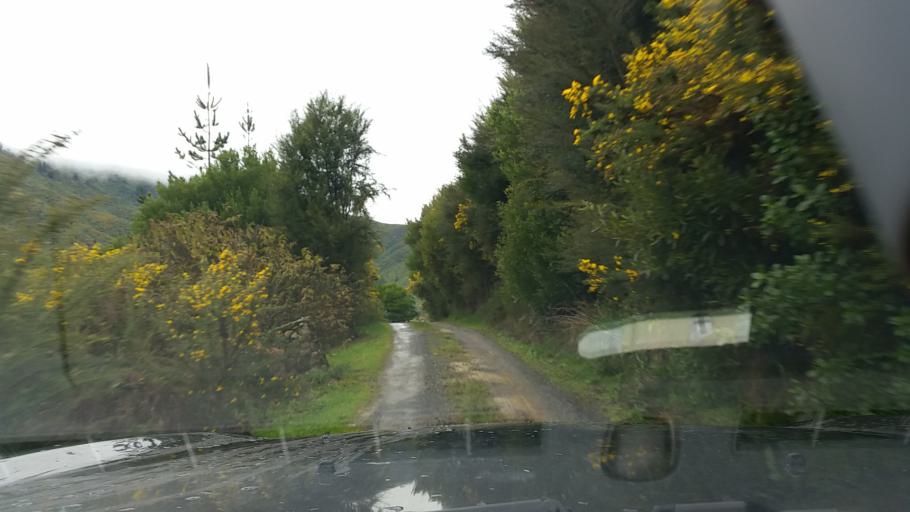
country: NZ
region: Marlborough
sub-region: Marlborough District
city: Picton
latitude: -41.2638
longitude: 174.0371
